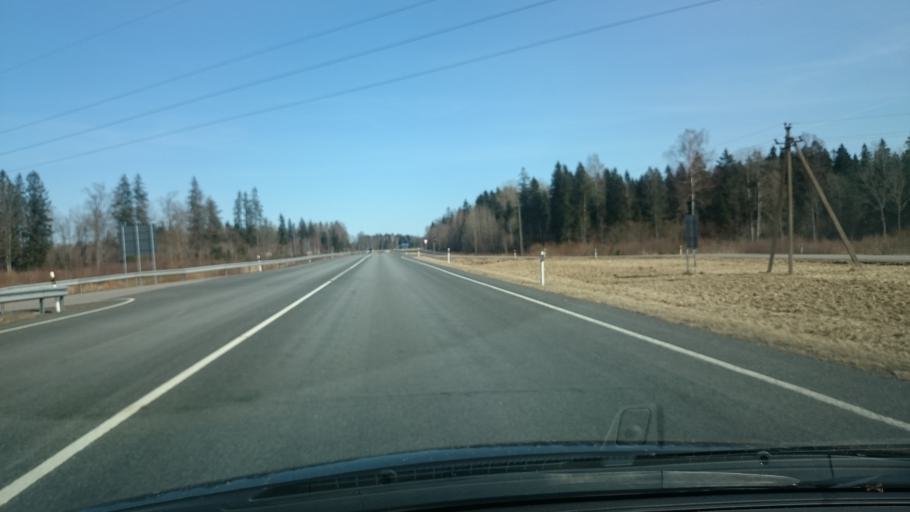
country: EE
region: Paernumaa
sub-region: Vaendra vald (alev)
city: Vandra
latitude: 58.6636
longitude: 25.0281
